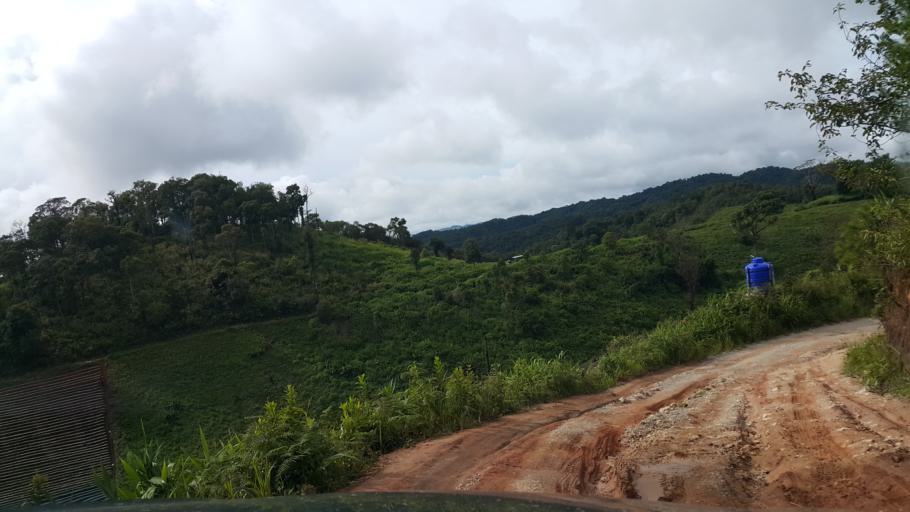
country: TH
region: Chiang Mai
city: Samoeng
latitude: 18.8700
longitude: 98.4975
